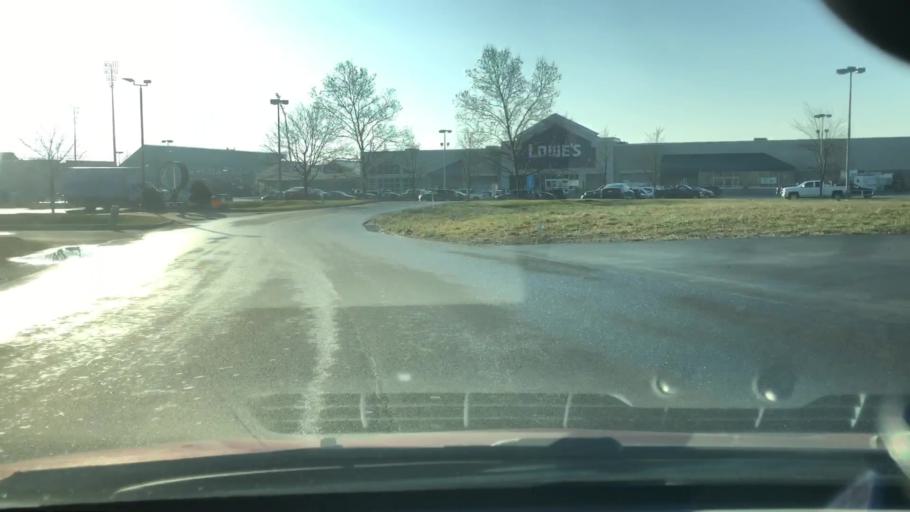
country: US
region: Ohio
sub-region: Franklin County
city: Columbus
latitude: 40.0126
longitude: -82.9946
